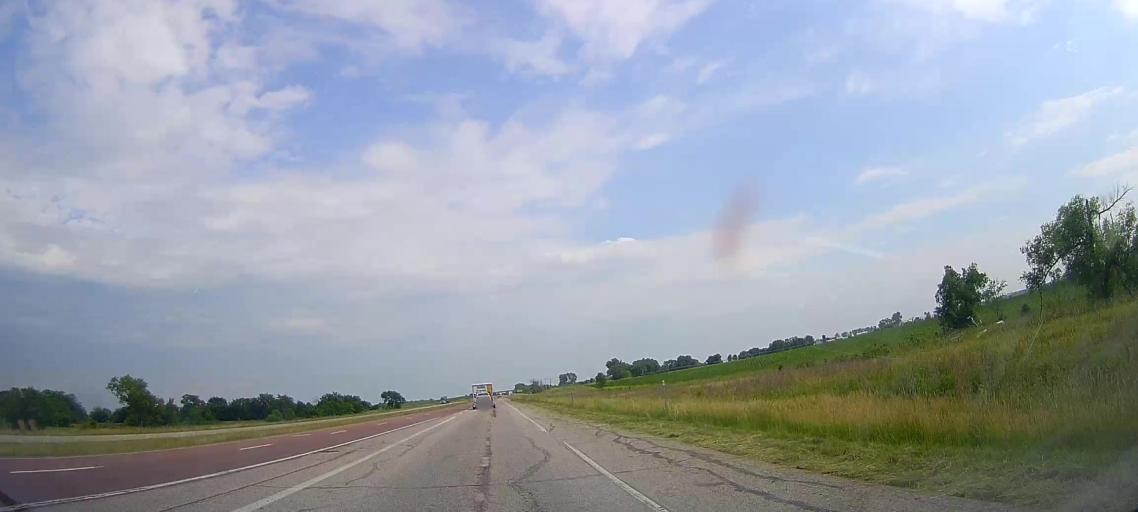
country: US
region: Iowa
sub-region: Monona County
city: Onawa
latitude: 41.9897
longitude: -96.1097
